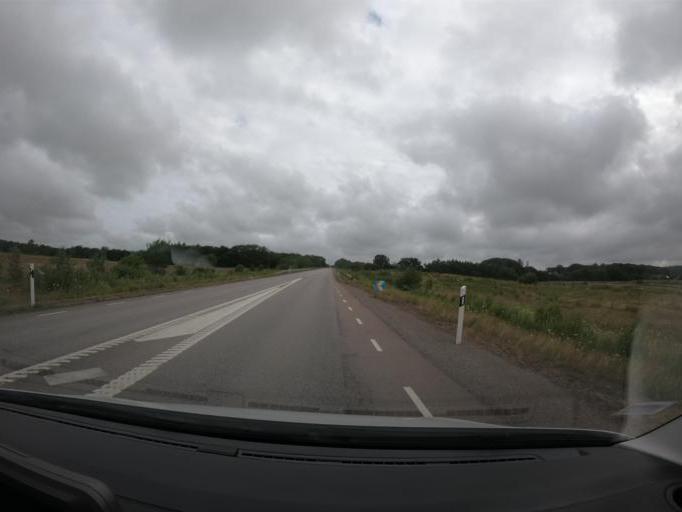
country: SE
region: Skane
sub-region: Bastads Kommun
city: Forslov
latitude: 56.3597
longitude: 12.8012
